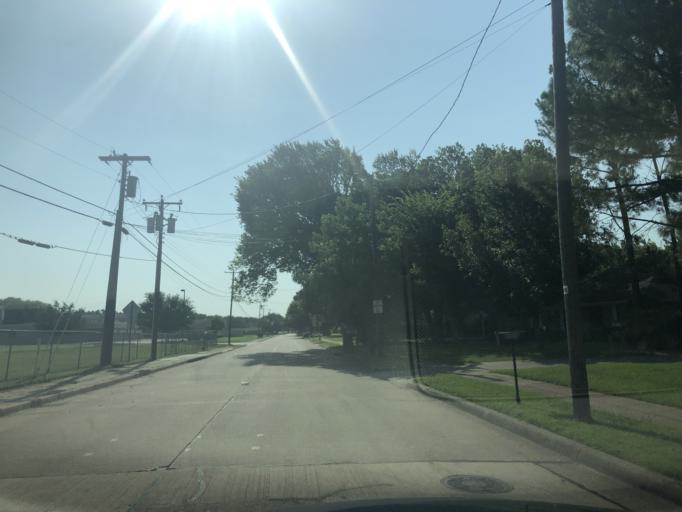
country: US
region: Texas
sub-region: Dallas County
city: Irving
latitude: 32.8120
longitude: -96.9850
